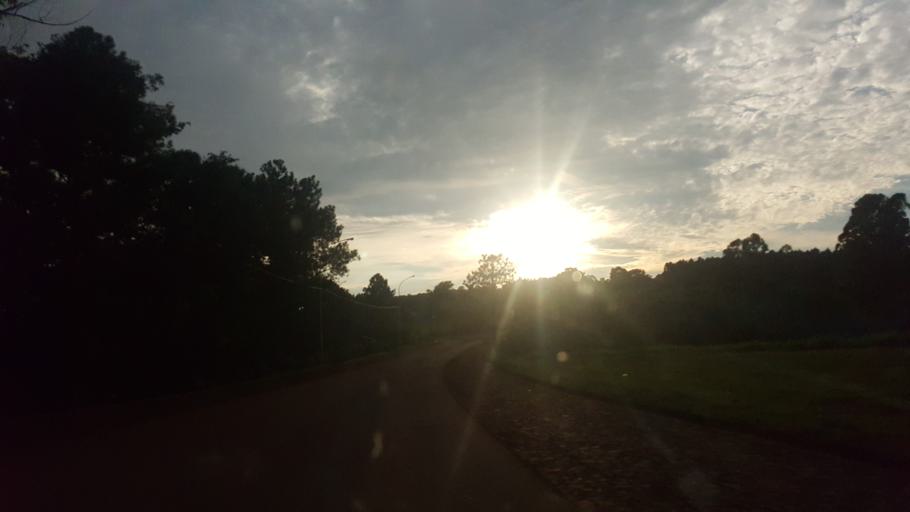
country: AR
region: Misiones
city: Dos de Mayo
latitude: -27.0358
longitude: -54.6779
